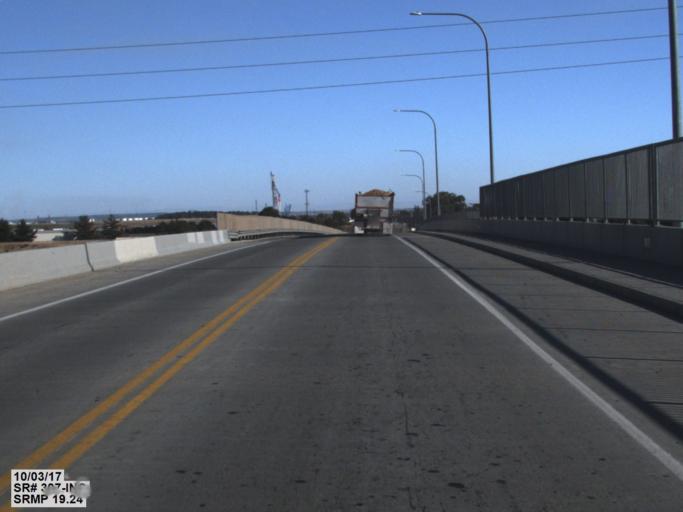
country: US
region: Washington
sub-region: Franklin County
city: Pasco
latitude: 46.2219
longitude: -119.0925
